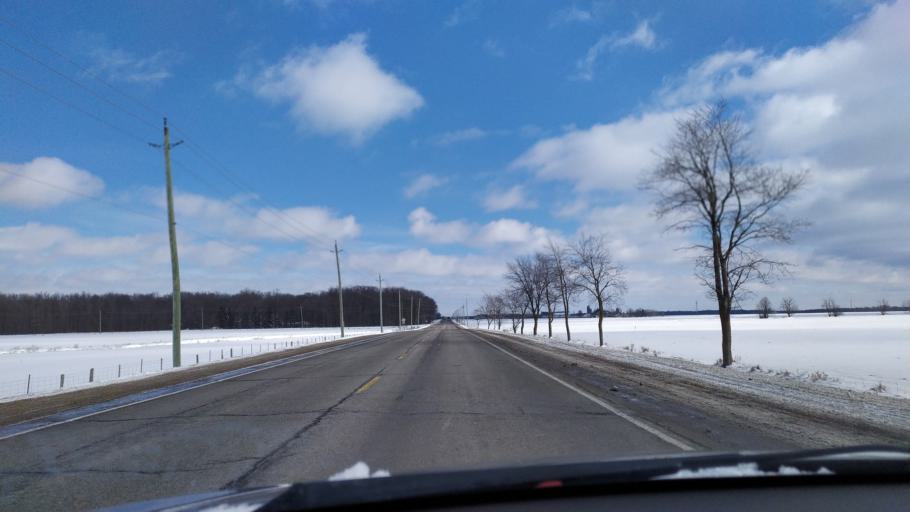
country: CA
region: Ontario
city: Waterloo
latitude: 43.5792
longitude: -80.5945
